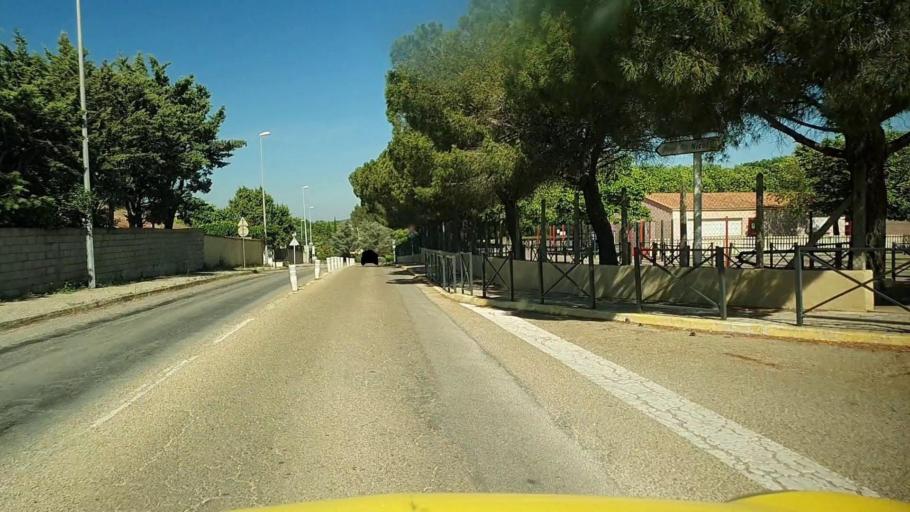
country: FR
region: Languedoc-Roussillon
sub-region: Departement du Gard
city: Poulx
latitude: 43.9101
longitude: 4.4197
